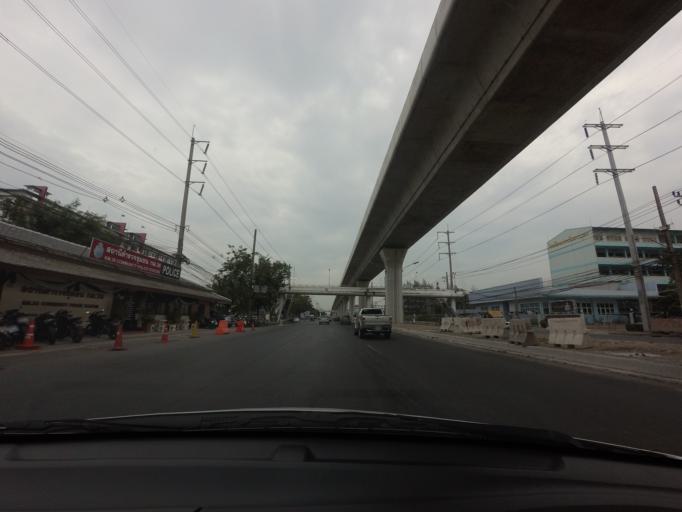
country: TH
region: Samut Prakan
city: Samut Prakan
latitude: 13.5665
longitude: 100.6084
